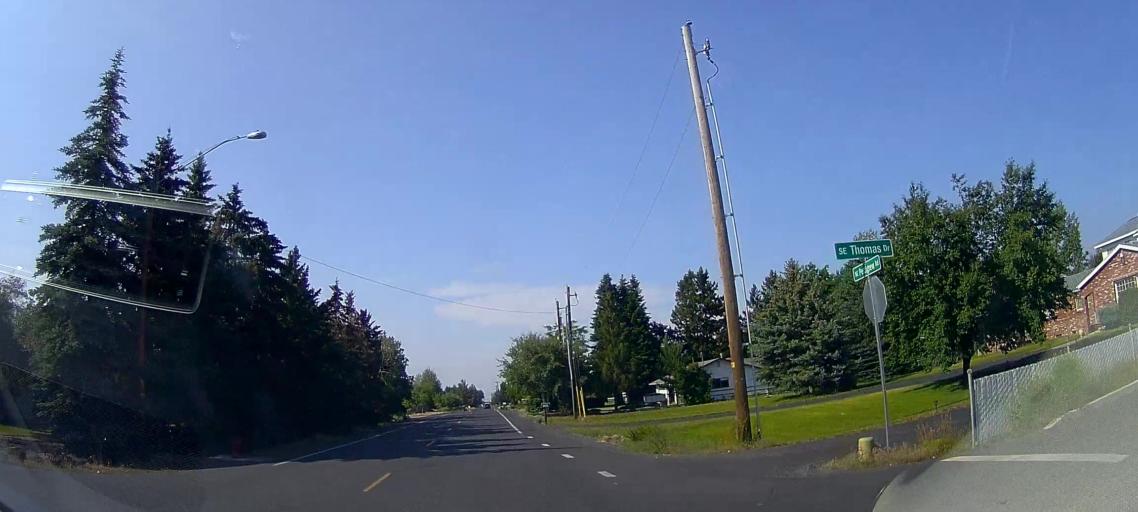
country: US
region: Oregon
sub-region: Deschutes County
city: Bend
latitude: 44.0450
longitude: -121.2686
